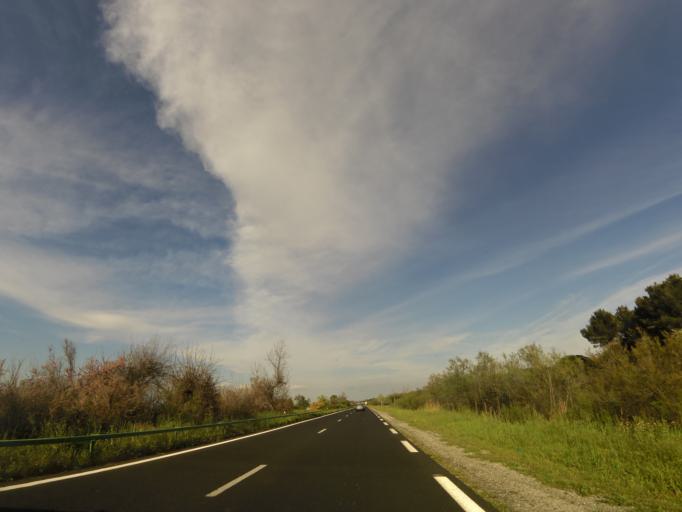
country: FR
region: Languedoc-Roussillon
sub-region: Departement de l'Herault
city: La Grande-Motte
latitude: 43.5676
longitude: 4.0651
